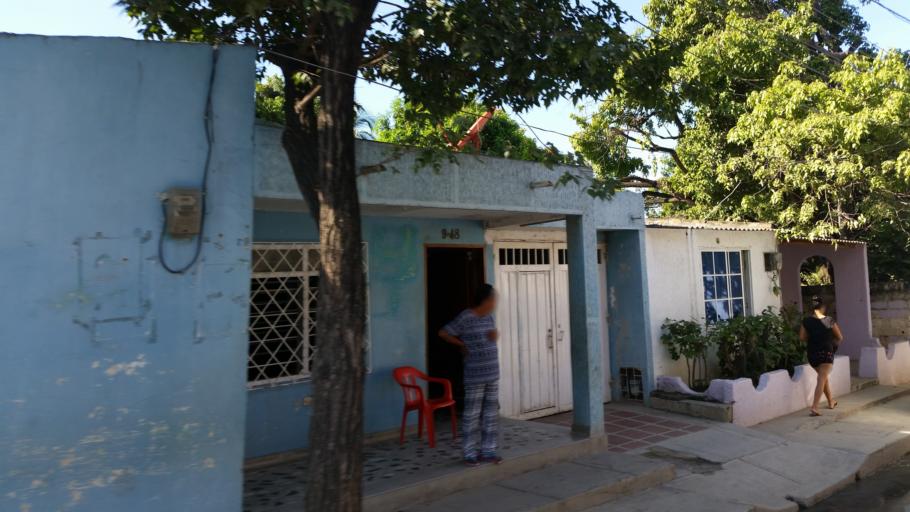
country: CO
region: Magdalena
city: Santa Marta
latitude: 11.1490
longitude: -74.2199
